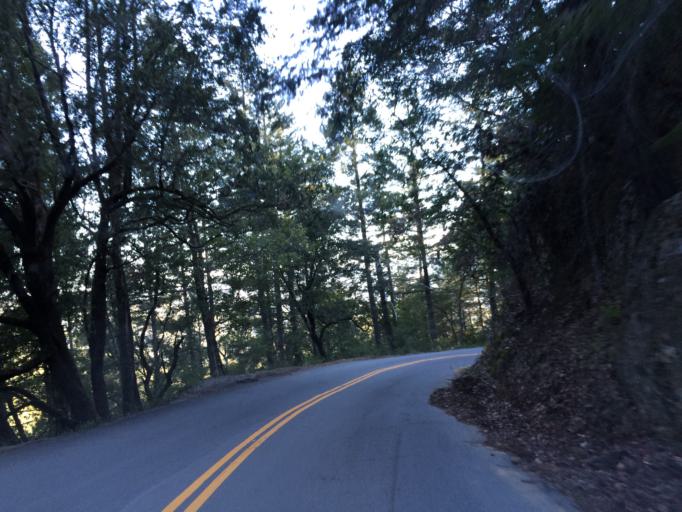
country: US
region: California
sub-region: Santa Cruz County
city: Boulder Creek
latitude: 37.1465
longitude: -122.1803
